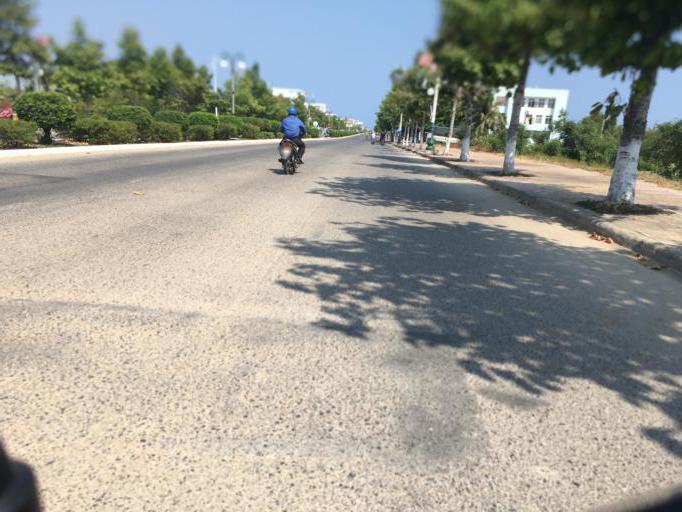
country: VN
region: Ninh Thuan
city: Phan Rang-Thap Cham
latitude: 11.5646
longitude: 109.0052
